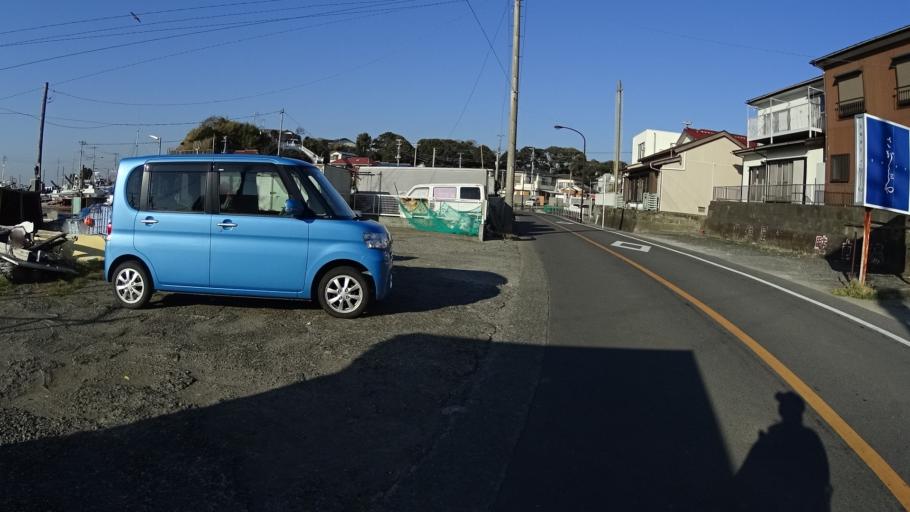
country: JP
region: Kanagawa
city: Miura
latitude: 35.2001
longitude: 139.6068
